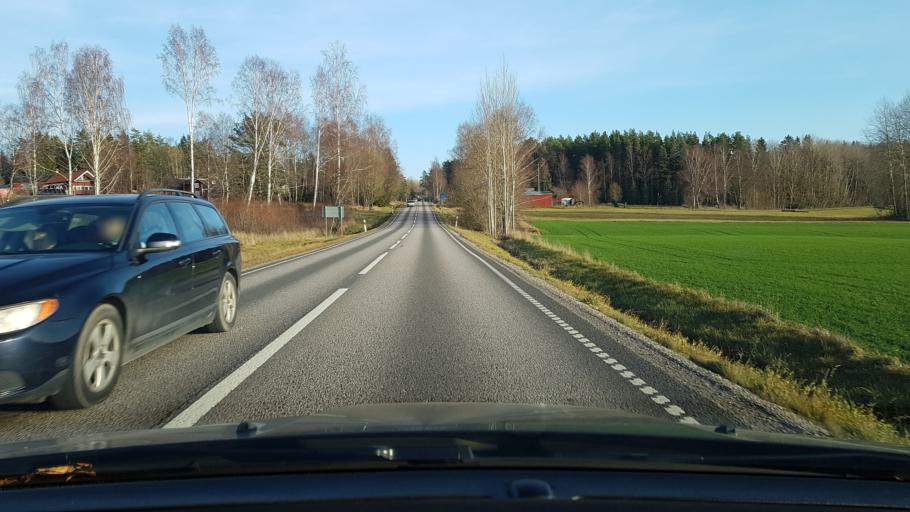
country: SE
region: Stockholm
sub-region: Norrtalje Kommun
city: Nykvarn
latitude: 59.7407
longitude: 18.1986
